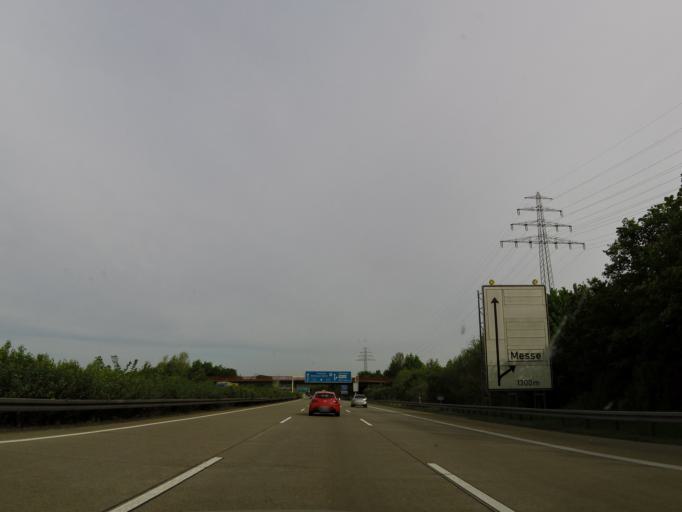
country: DE
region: Lower Saxony
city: Sarstedt
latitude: 52.2886
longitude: 9.9002
